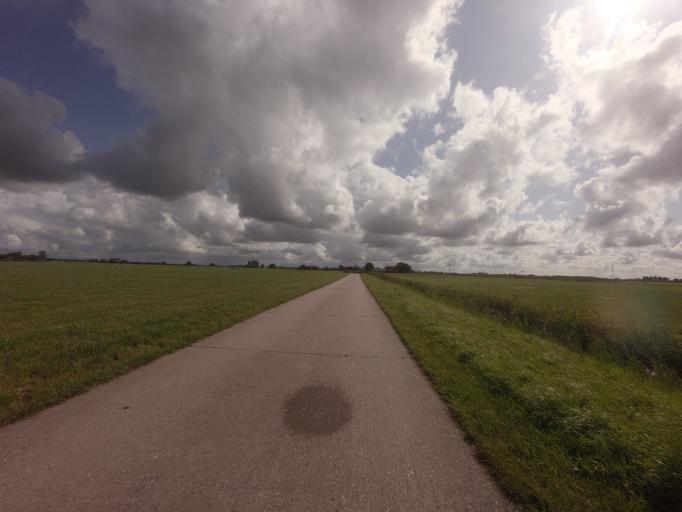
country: NL
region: Friesland
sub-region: Sudwest Fryslan
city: Scharnegoutum
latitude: 53.0682
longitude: 5.6394
